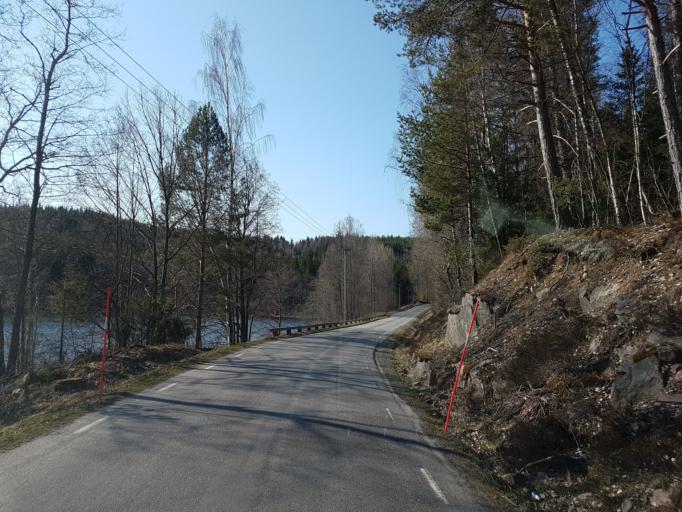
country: SE
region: Kalmar
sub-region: Vasterviks Kommun
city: Overum
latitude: 58.1750
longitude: 16.2766
